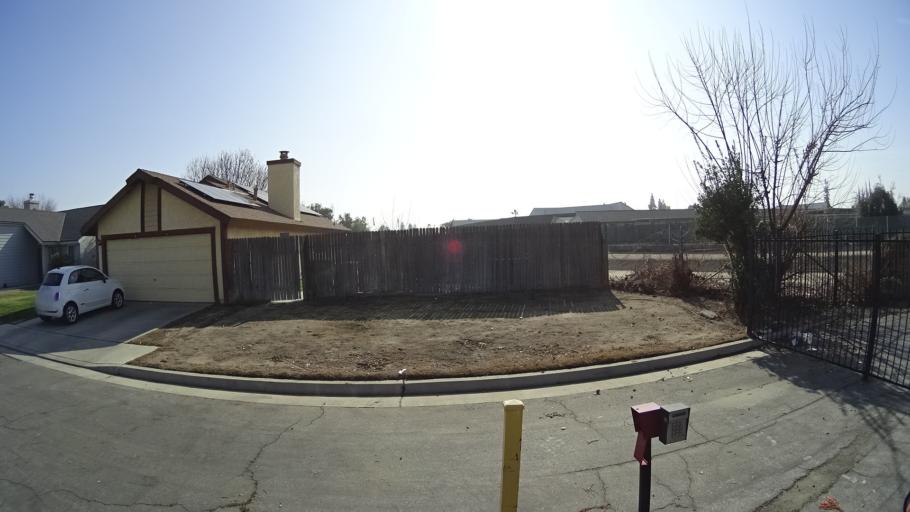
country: US
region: California
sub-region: Kern County
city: Bakersfield
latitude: 35.3196
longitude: -119.0553
